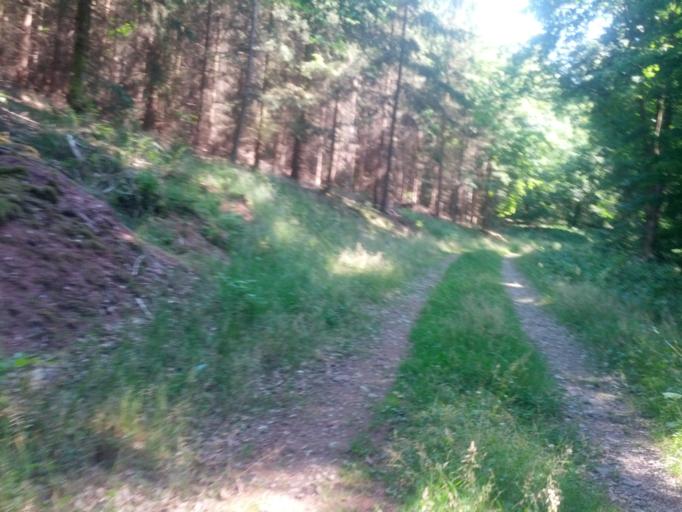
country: DE
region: Thuringia
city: Eisenach
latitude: 50.9720
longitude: 10.2809
